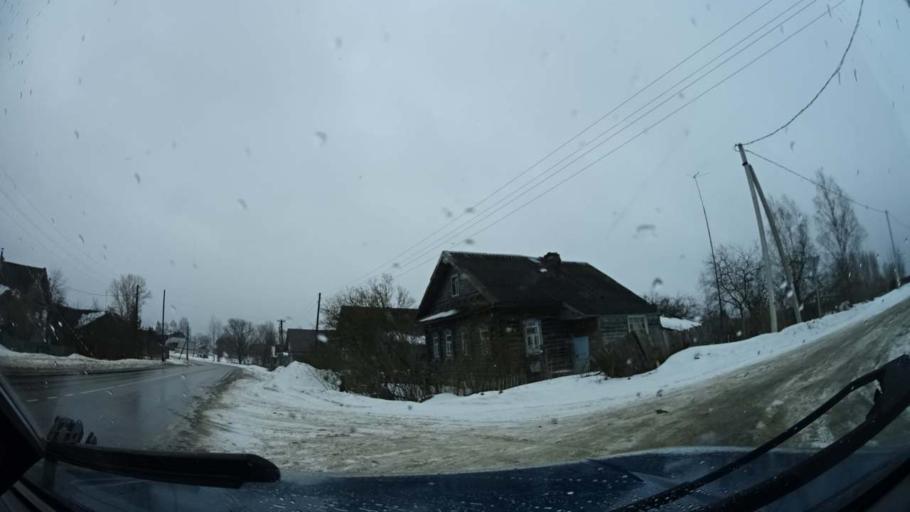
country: RU
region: Tverskaya
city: Radchenko
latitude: 56.8550
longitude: 36.5496
